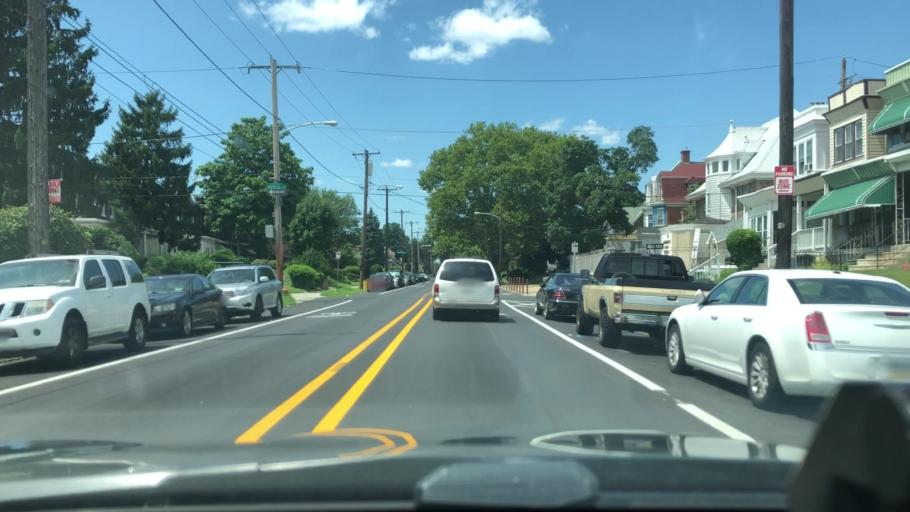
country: US
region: Pennsylvania
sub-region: Montgomery County
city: Wyndmoor
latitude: 40.0459
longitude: -75.1655
